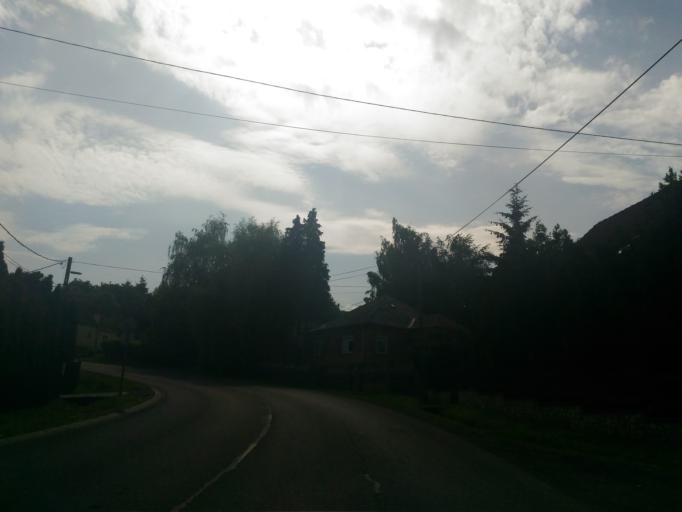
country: HU
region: Baranya
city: Komlo
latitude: 46.1600
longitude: 18.2353
